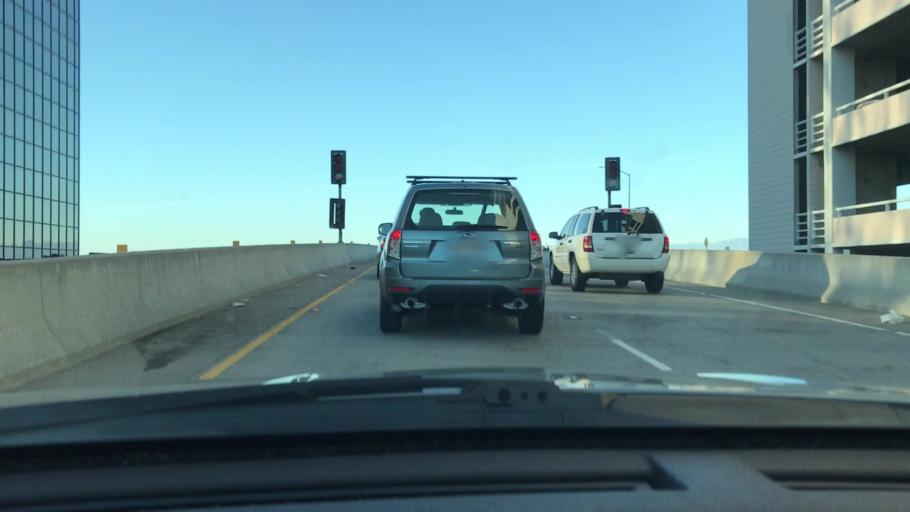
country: US
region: California
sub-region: Los Angeles County
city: Del Aire
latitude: 33.9298
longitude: -118.3852
